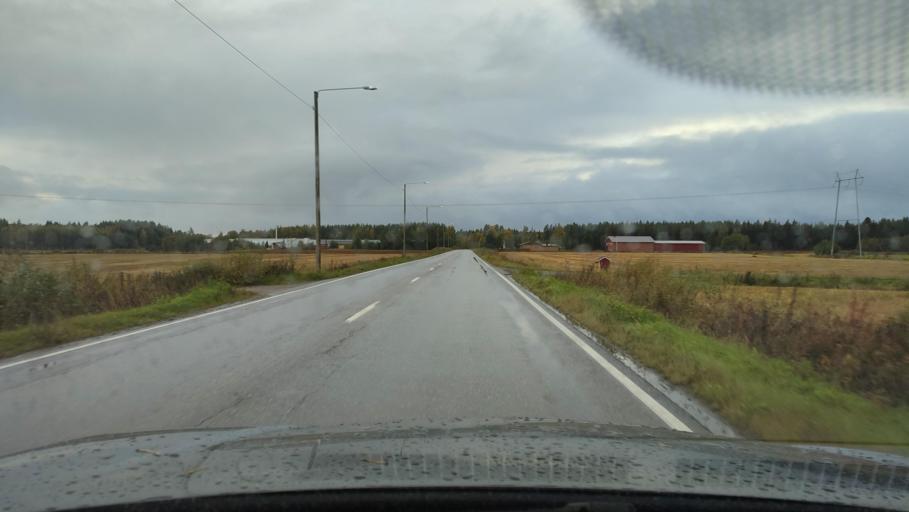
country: FI
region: Southern Ostrobothnia
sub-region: Suupohja
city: Karijoki
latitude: 62.2371
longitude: 21.6109
